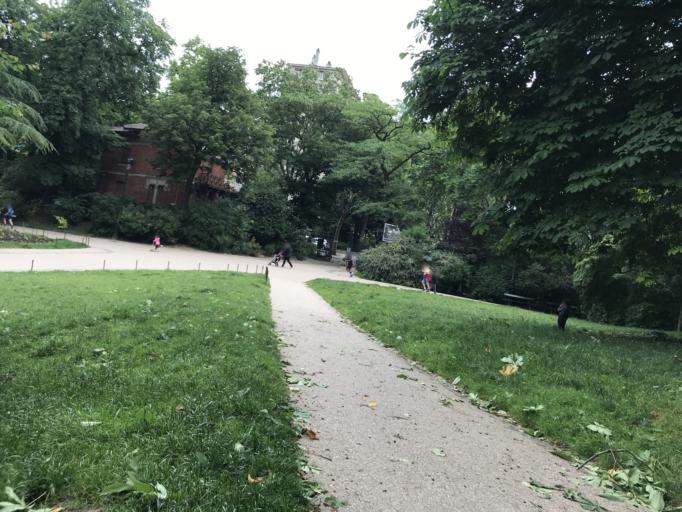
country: FR
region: Ile-de-France
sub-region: Departement de Seine-Saint-Denis
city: Le Pre-Saint-Gervais
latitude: 48.8778
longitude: 2.3804
